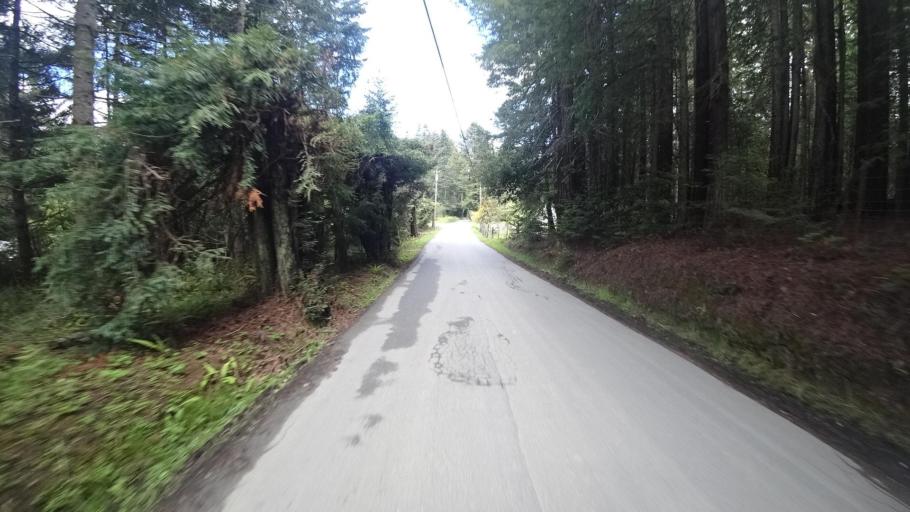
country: US
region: California
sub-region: Humboldt County
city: Blue Lake
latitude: 40.8984
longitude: -123.9957
